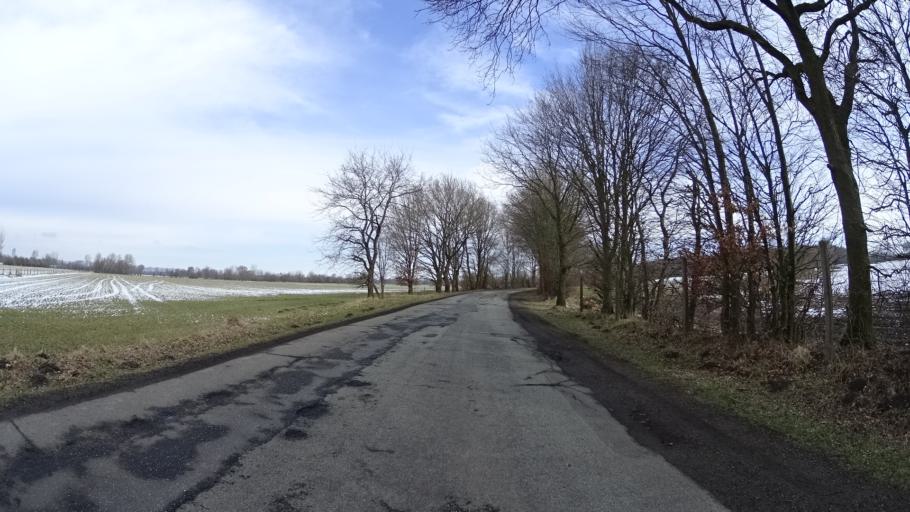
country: DE
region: Schleswig-Holstein
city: Gonnebek
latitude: 54.0493
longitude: 10.1313
